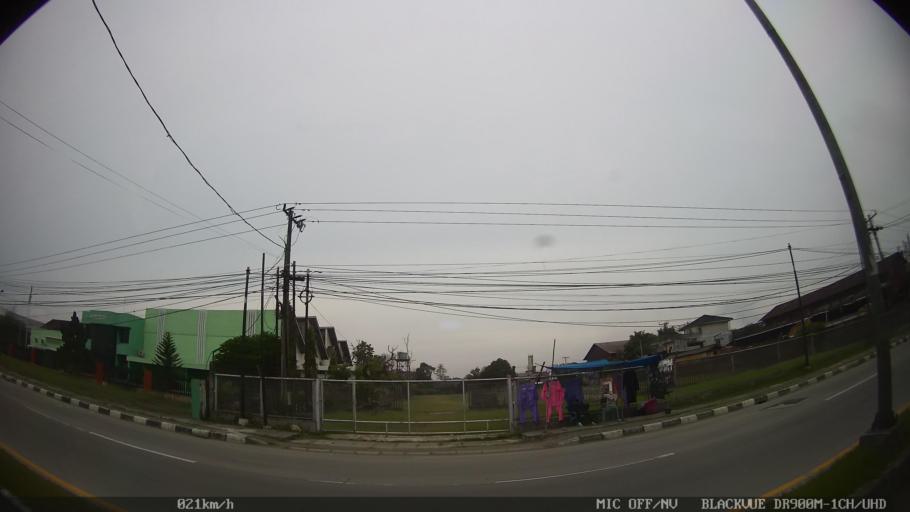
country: ID
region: North Sumatra
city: Deli Tua
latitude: 3.5323
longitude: 98.7258
